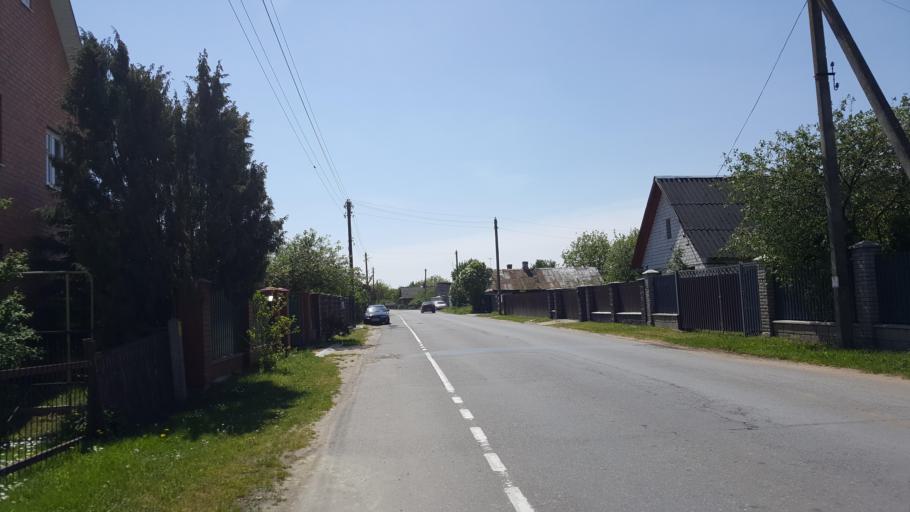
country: BY
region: Brest
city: Charnawchytsy
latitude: 52.2237
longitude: 23.7386
